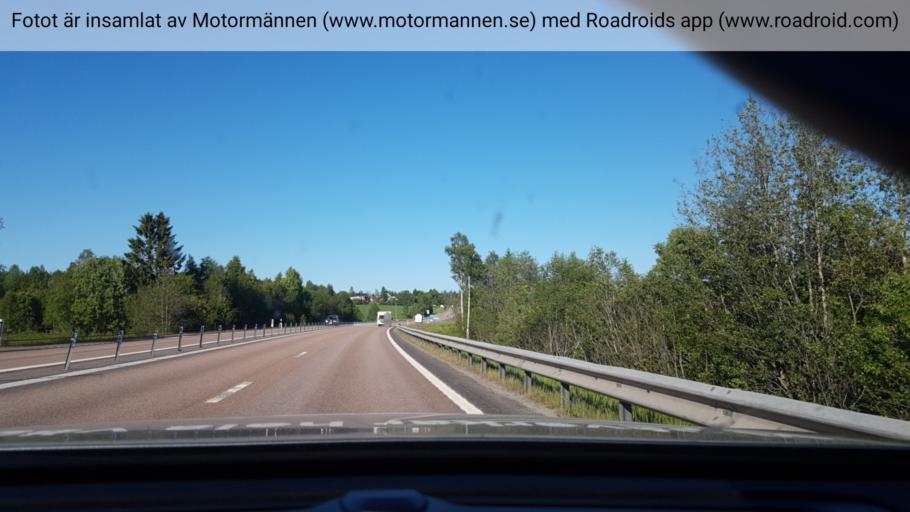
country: SE
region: Vaesternorrland
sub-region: Haernoesands Kommun
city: Haernoesand
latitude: 62.5825
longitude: 17.7688
